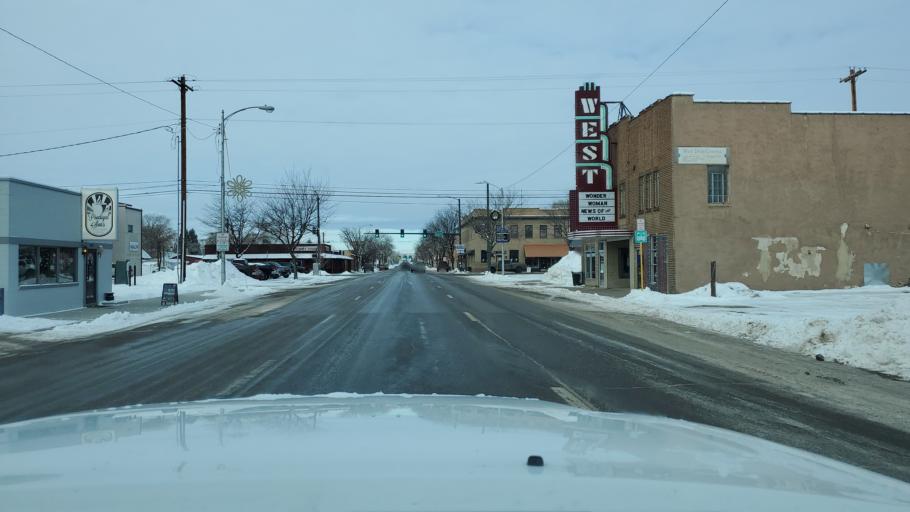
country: US
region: Colorado
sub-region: Moffat County
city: Craig
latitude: 40.5143
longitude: -107.5461
